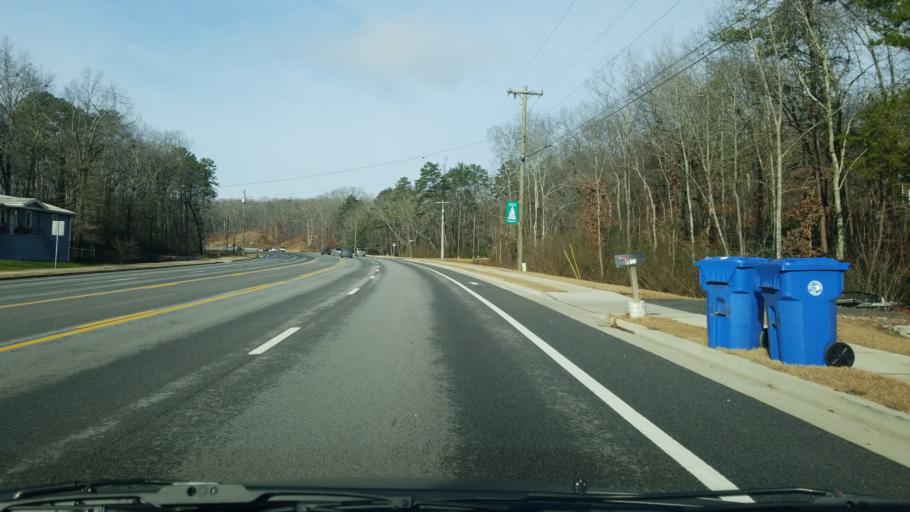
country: US
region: Tennessee
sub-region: Hamilton County
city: Collegedale
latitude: 35.0675
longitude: -85.0832
